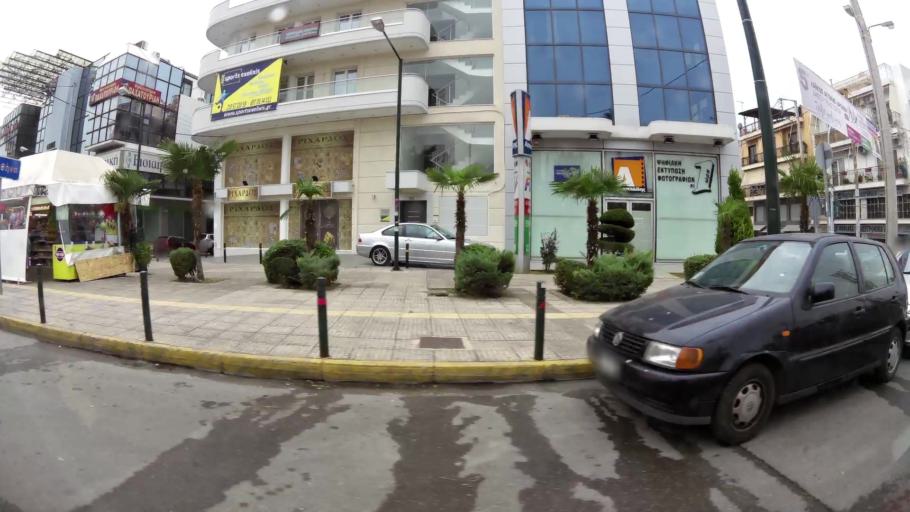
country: GR
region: Attica
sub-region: Nomarchia Athinas
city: Peristeri
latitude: 38.0148
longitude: 23.6932
